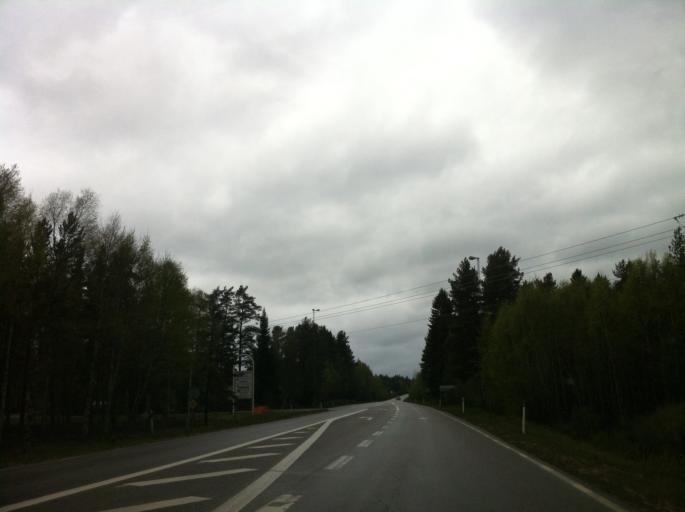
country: SE
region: Jaemtland
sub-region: Harjedalens Kommun
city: Sveg
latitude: 62.0460
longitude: 14.3443
